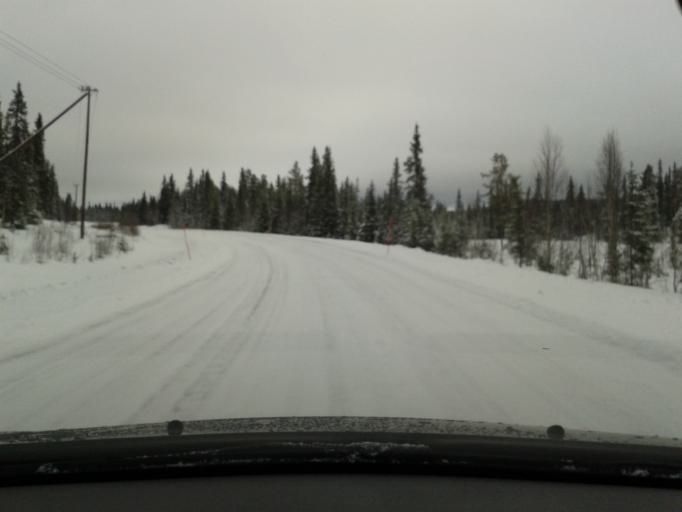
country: SE
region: Vaesterbotten
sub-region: Vilhelmina Kommun
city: Sjoberg
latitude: 65.2352
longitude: 15.8381
